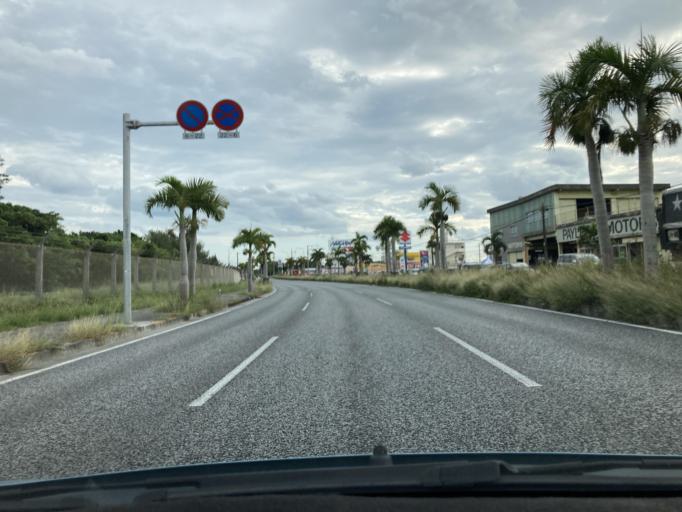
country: JP
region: Okinawa
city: Chatan
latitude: 26.3549
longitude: 127.7455
